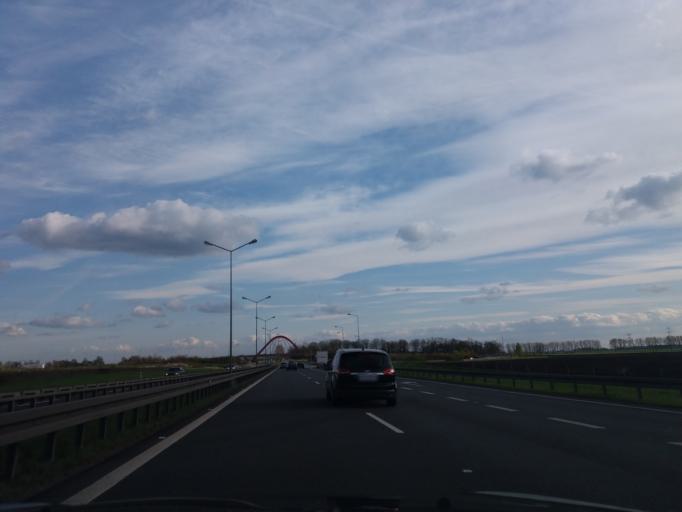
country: PL
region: Lower Silesian Voivodeship
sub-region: Powiat wroclawski
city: Zorawina
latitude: 50.9741
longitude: 17.0627
